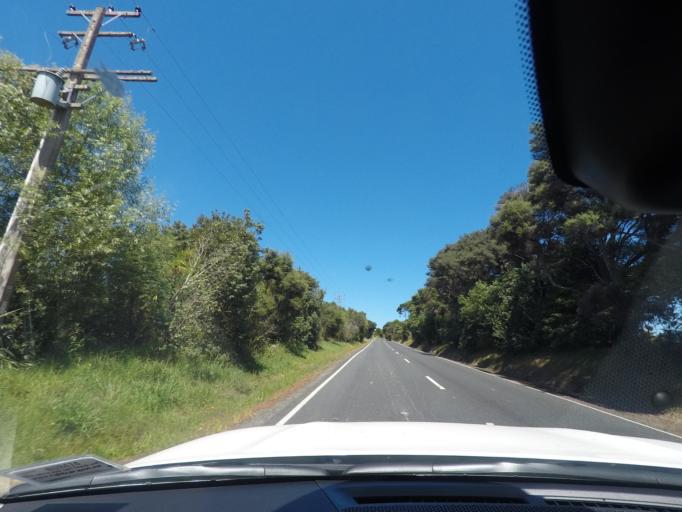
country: NZ
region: Auckland
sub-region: Auckland
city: Parakai
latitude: -36.5717
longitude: 174.3707
